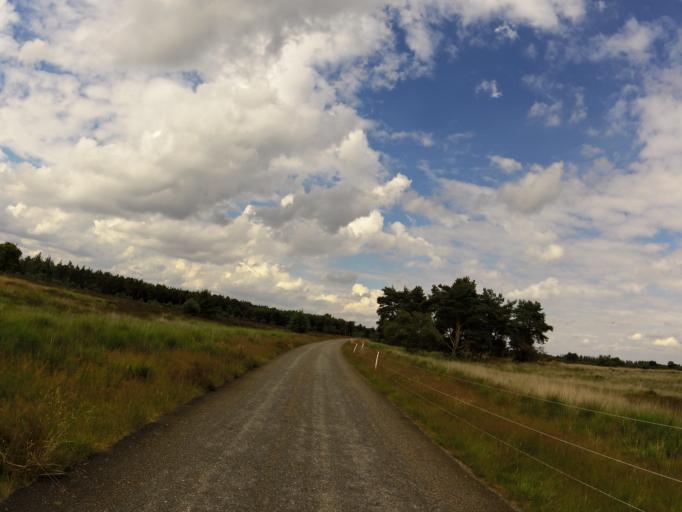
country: NL
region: North Brabant
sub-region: Gemeente Valkenswaard
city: Valkenswaard
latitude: 51.3068
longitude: 5.5068
